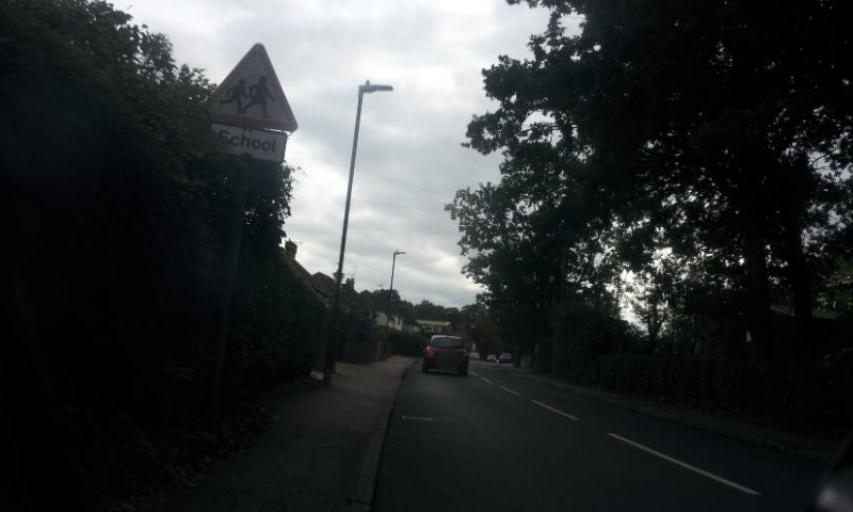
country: GB
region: England
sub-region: Kent
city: Tonbridge
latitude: 51.2183
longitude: 0.2425
